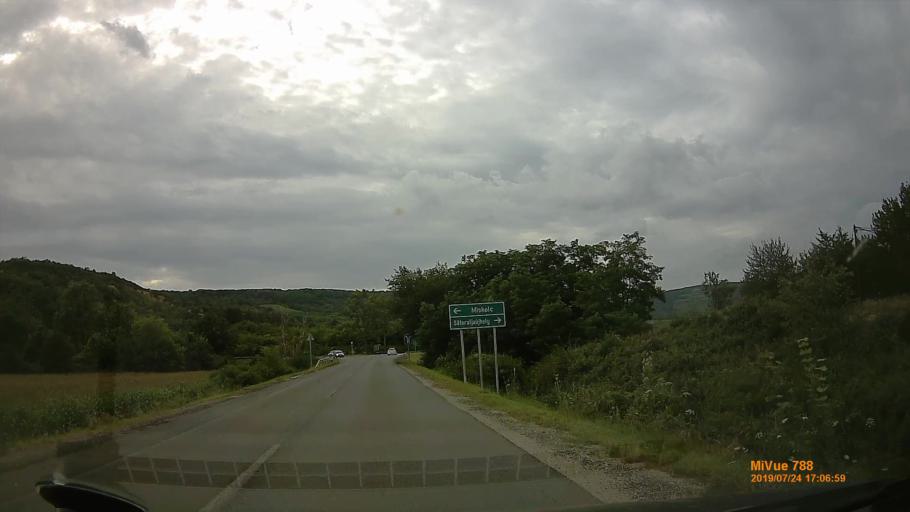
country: HU
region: Borsod-Abauj-Zemplen
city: Tarcal
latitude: 48.1744
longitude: 21.3485
